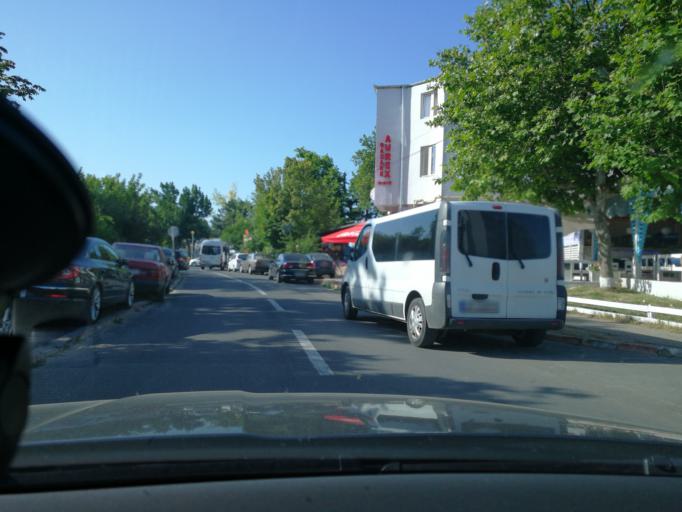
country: RO
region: Constanta
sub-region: Municipiul Mangalia
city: Mangalia
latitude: 43.8463
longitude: 28.5995
